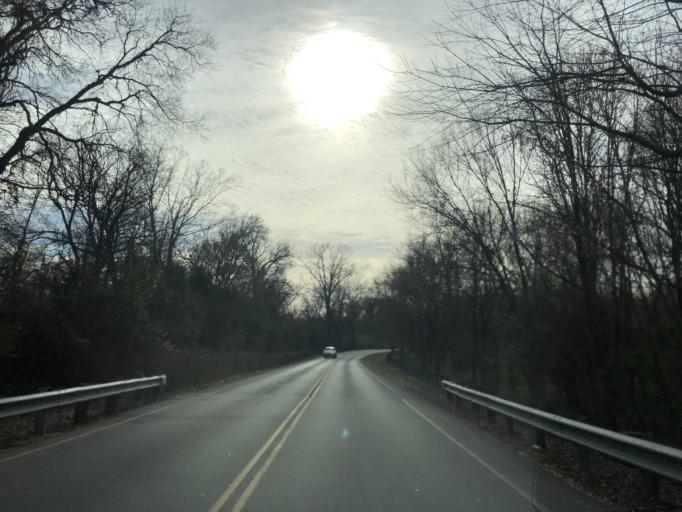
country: US
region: Tennessee
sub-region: Williamson County
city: Franklin
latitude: 35.9678
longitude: -86.9008
